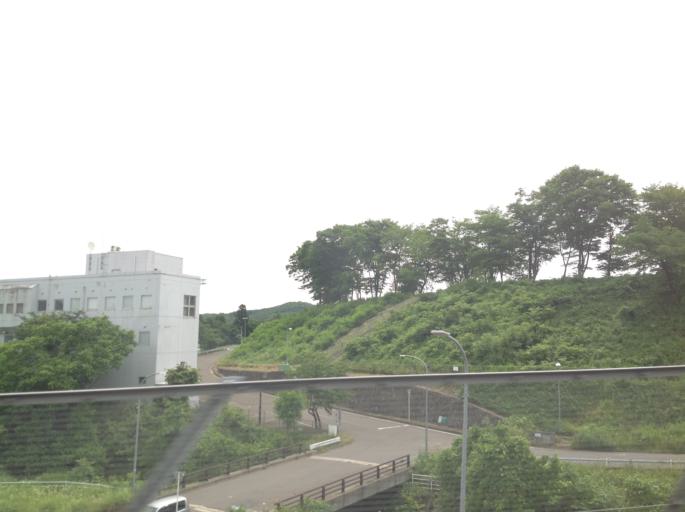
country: JP
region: Miyagi
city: Sendai
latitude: 38.2607
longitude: 140.8108
